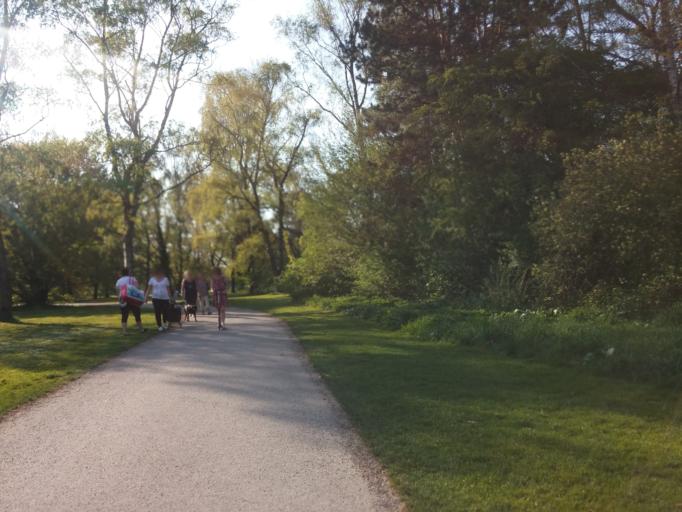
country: DE
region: Bavaria
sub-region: Upper Bavaria
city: Neubiberg
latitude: 48.1107
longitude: 11.6522
